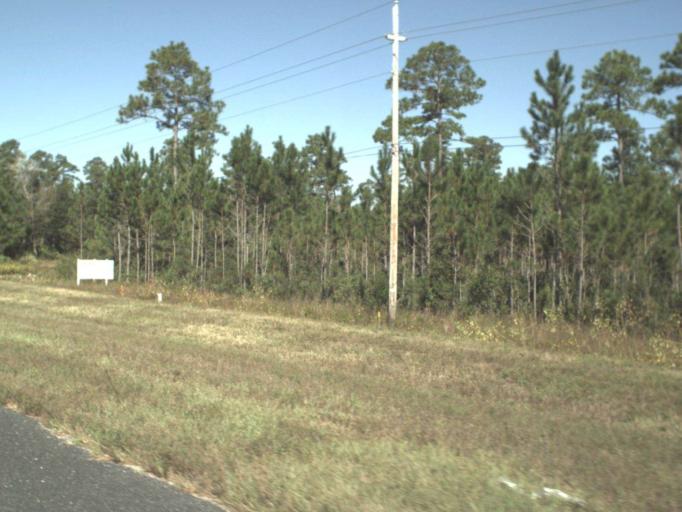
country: US
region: Florida
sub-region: Walton County
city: Seaside
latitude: 30.3724
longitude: -86.2067
